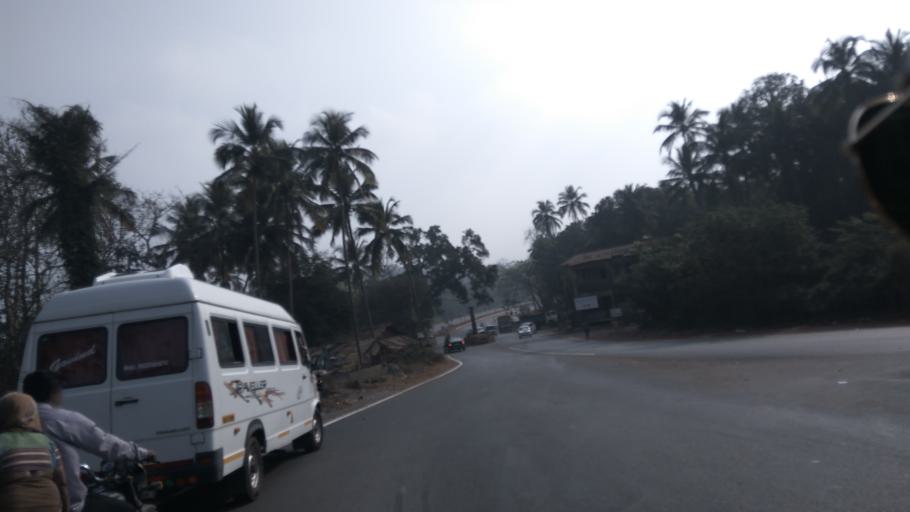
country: IN
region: Goa
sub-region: North Goa
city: Jua
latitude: 15.4990
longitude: 73.9127
